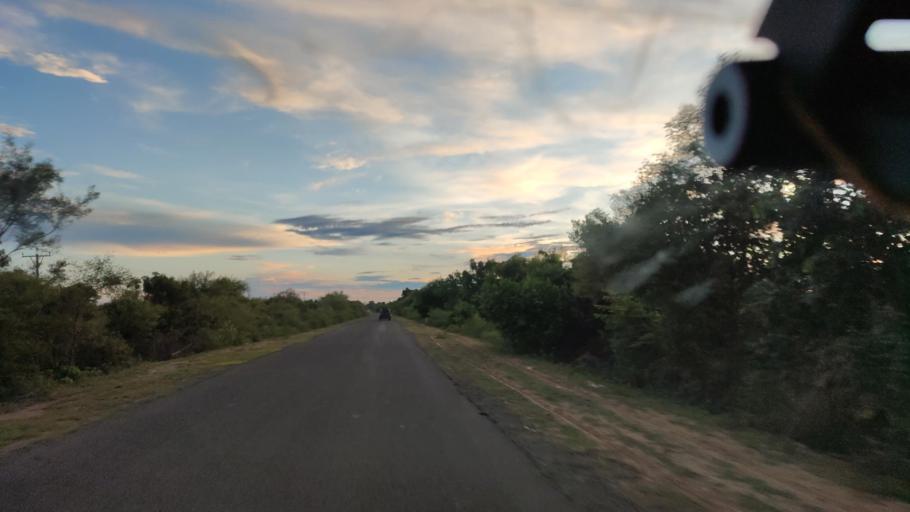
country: MM
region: Magway
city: Taungdwingyi
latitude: 20.1531
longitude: 95.5309
